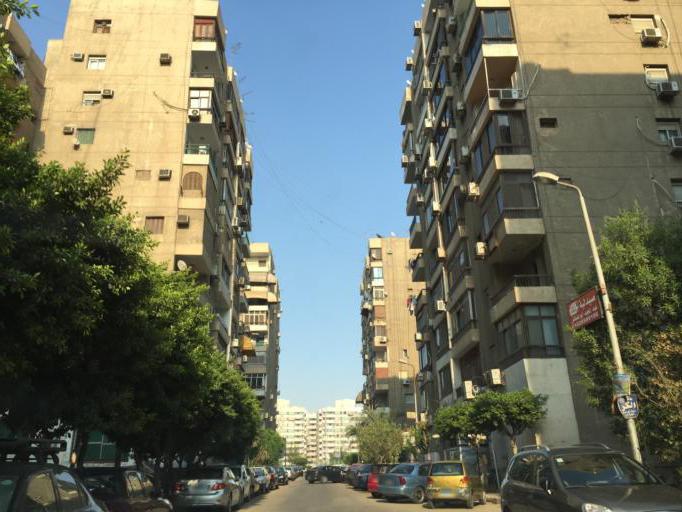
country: EG
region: Muhafazat al Qahirah
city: Cairo
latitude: 30.0720
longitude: 31.3373
